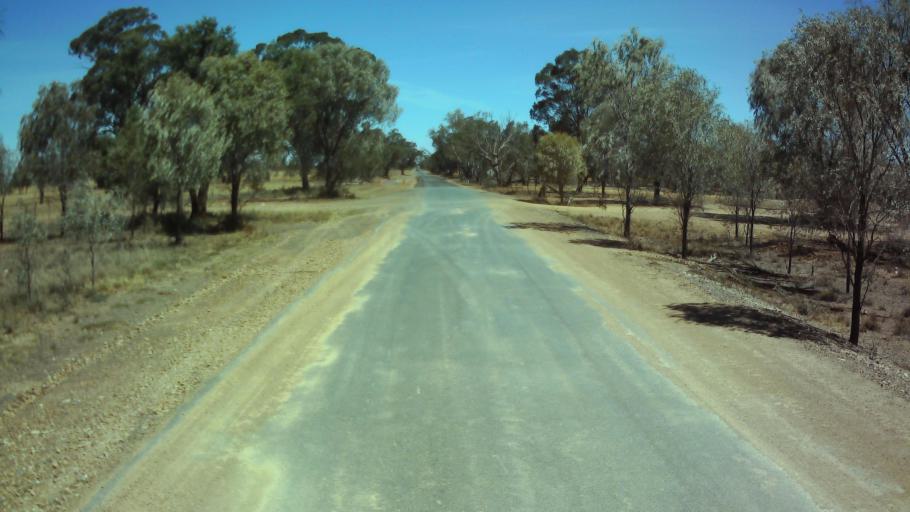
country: AU
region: New South Wales
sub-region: Weddin
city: Grenfell
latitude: -33.8412
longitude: 147.6973
